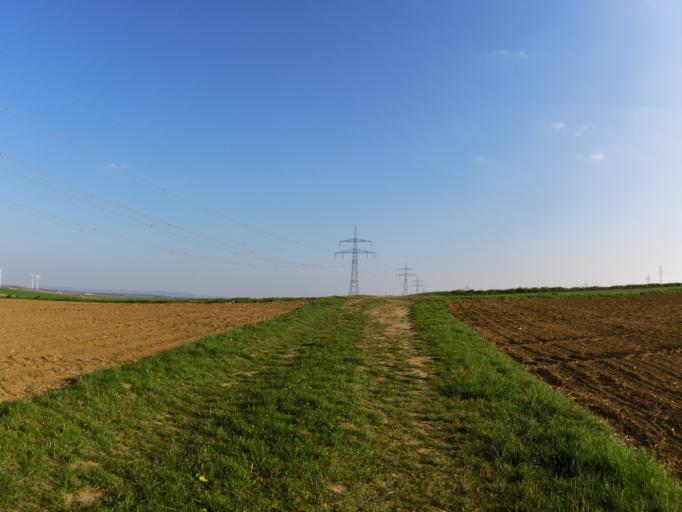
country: DE
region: Bavaria
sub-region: Regierungsbezirk Unterfranken
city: Theilheim
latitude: 49.7721
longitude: 10.0492
